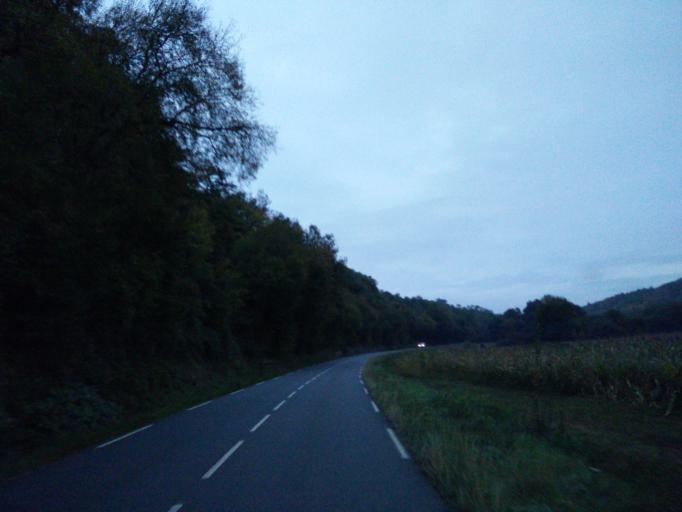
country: FR
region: Aquitaine
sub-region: Departement de la Dordogne
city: Saint-Cyprien
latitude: 44.9220
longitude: 1.0937
